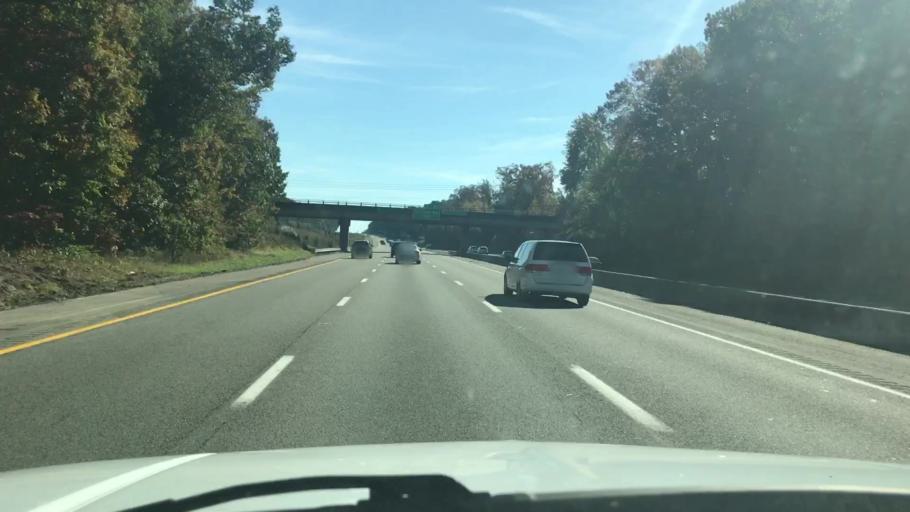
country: US
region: Virginia
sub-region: Henrico County
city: Tuckahoe
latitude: 37.6326
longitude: -77.5710
